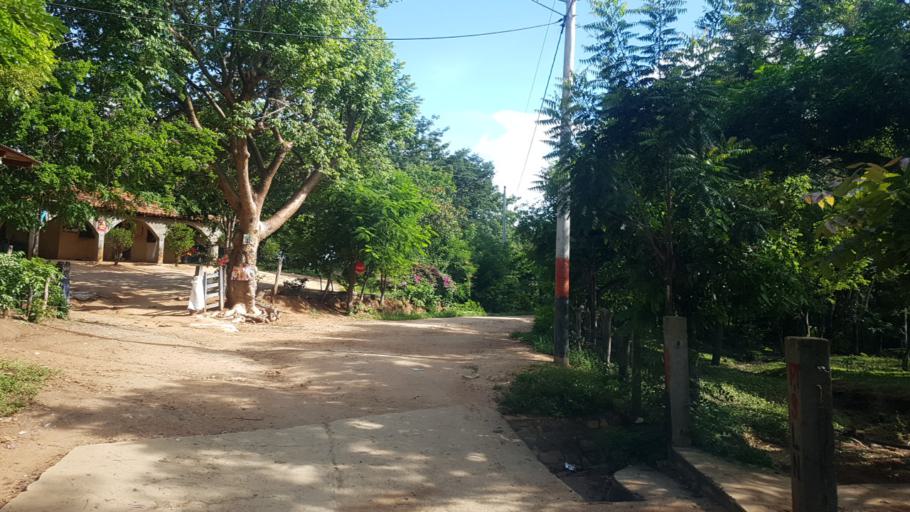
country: NI
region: Nueva Segovia
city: Mozonte
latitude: 13.6570
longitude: -86.3981
